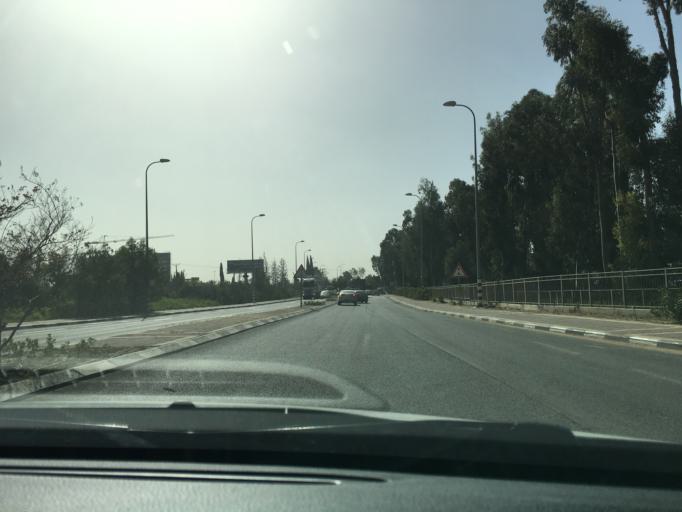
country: IL
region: Central District
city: Kfar Saba
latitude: 32.1726
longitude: 34.9311
